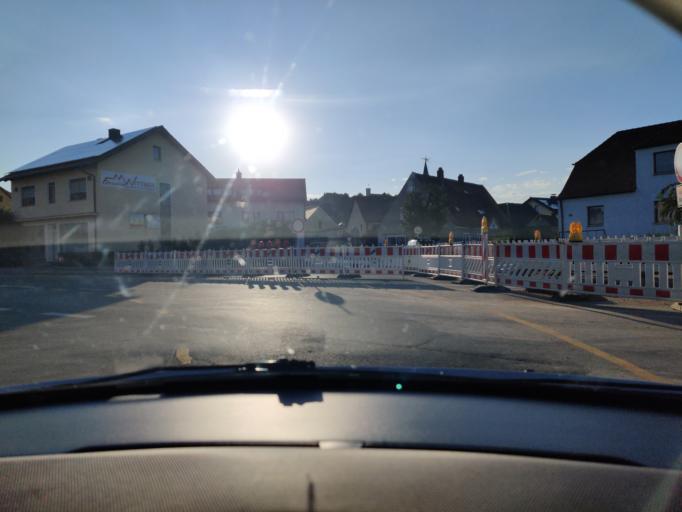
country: DE
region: Bavaria
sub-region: Upper Palatinate
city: Nabburg
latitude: 49.4533
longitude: 12.1868
